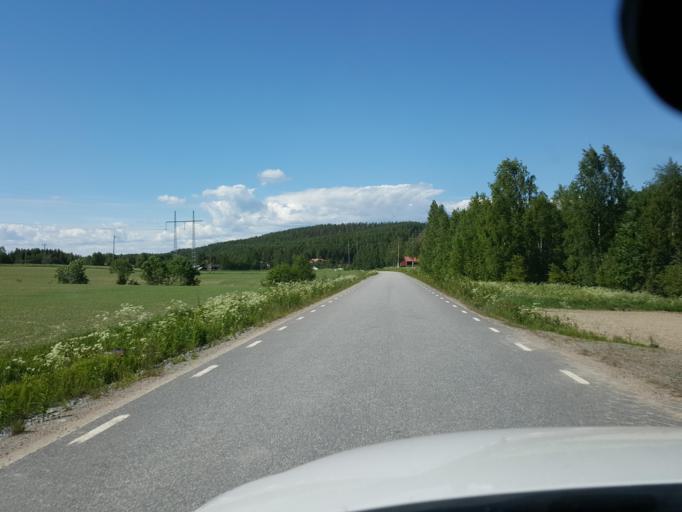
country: SE
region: Gaevleborg
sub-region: Ljusdals Kommun
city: Jaervsoe
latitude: 61.7429
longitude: 16.2722
